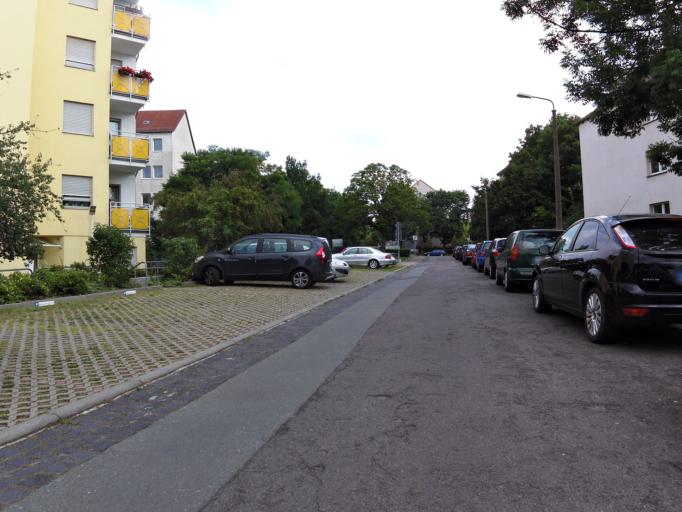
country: DE
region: Saxony
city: Leipzig
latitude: 51.3733
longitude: 12.3303
